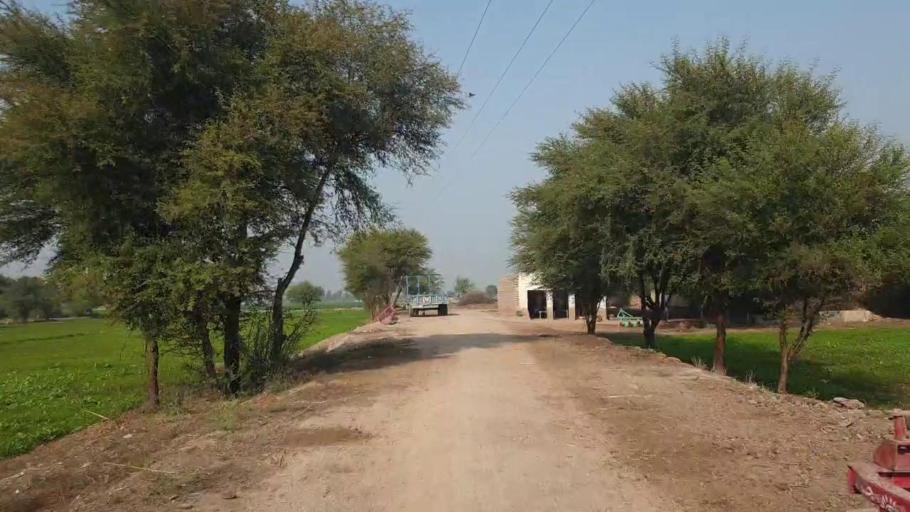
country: PK
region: Sindh
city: Shahdadpur
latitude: 26.0080
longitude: 68.5291
